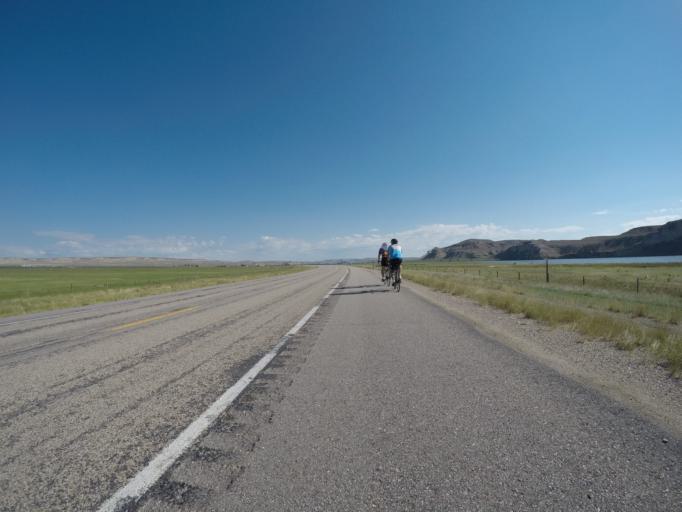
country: US
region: Wyoming
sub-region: Sublette County
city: Marbleton
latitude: 42.1399
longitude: -110.1852
